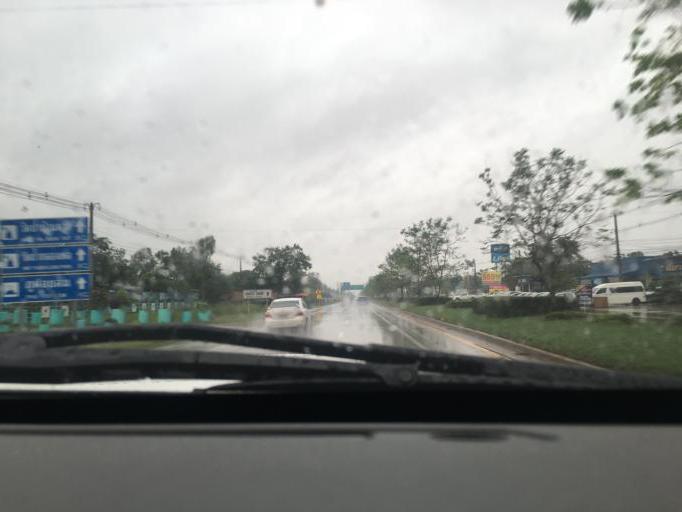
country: TH
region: Changwat Udon Thani
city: Udon Thani
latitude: 17.3845
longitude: 102.7568
